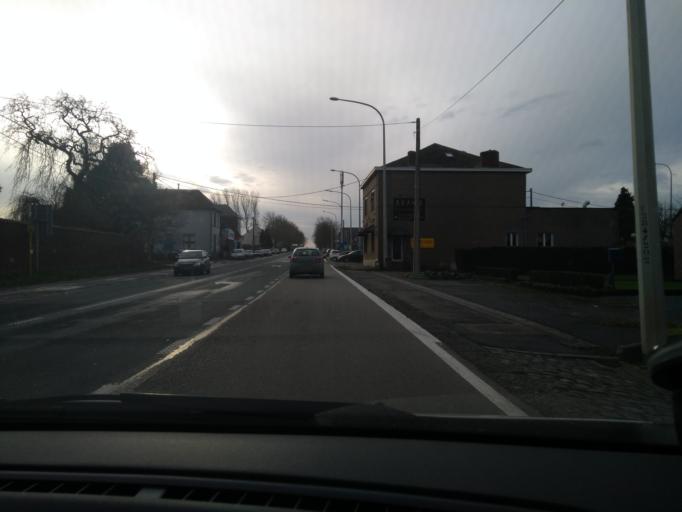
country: BE
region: Wallonia
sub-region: Province du Hainaut
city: Quevy-le-Petit
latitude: 50.3505
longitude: 3.9681
